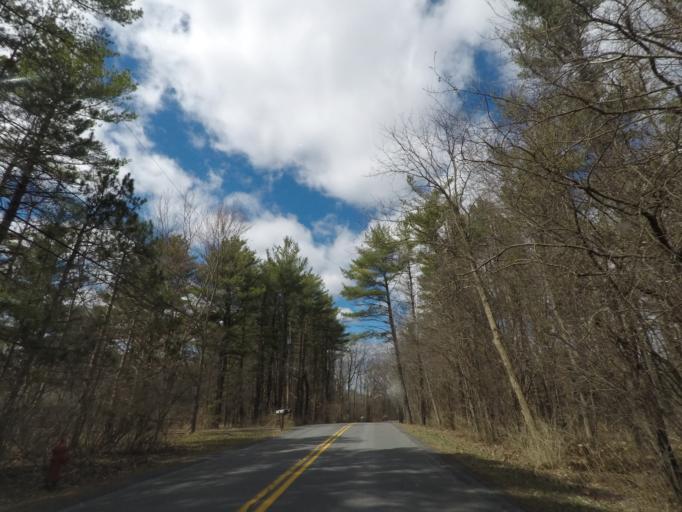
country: US
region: New York
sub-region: Albany County
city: Voorheesville
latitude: 42.6429
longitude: -73.9350
